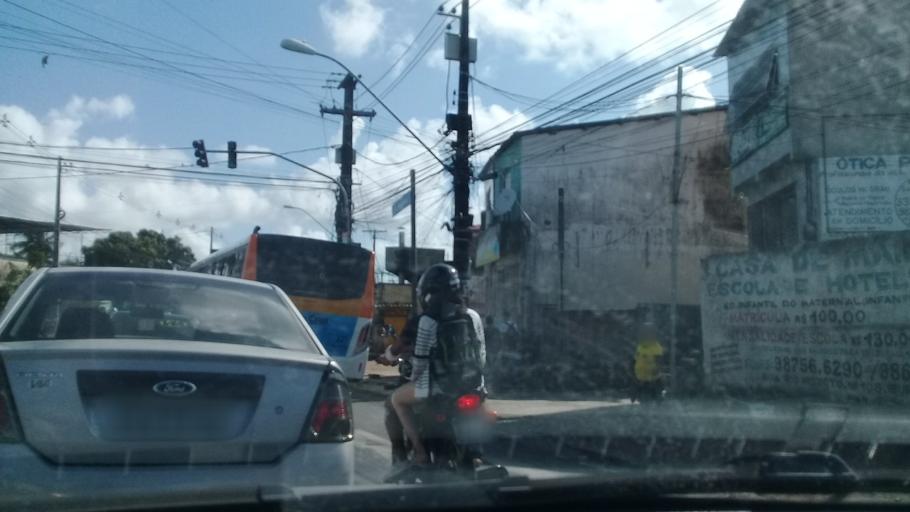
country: BR
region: Pernambuco
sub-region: Jaboatao Dos Guararapes
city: Jaboatao dos Guararapes
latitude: -8.1107
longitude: -34.9371
